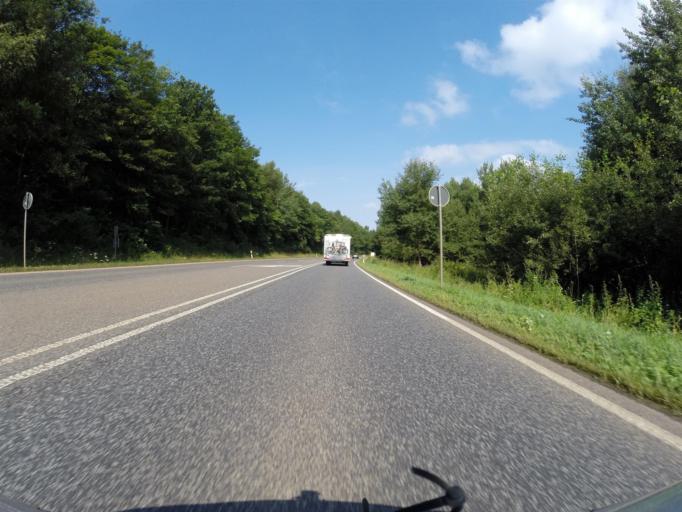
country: DE
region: Hesse
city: Hessisch Lichtenau
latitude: 51.2184
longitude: 9.6767
